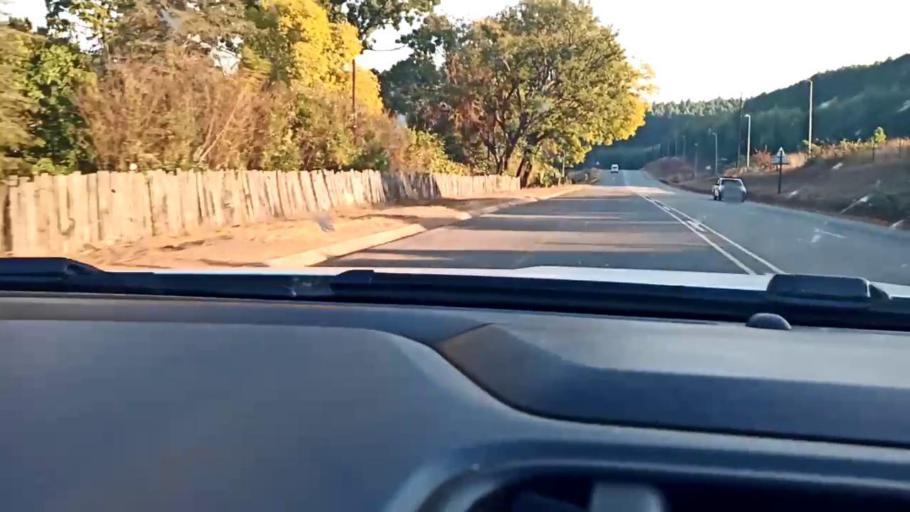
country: ZA
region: Limpopo
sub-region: Mopani District Municipality
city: Duiwelskloof
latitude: -23.7046
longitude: 30.1328
